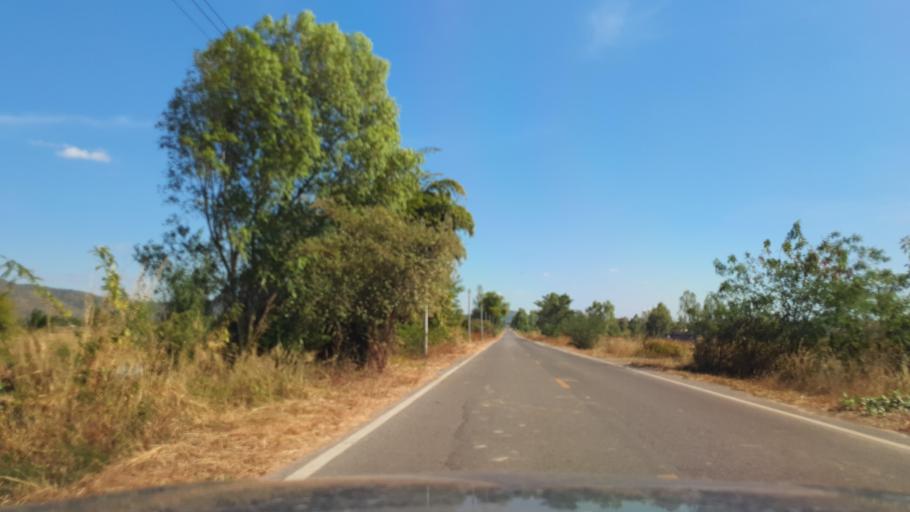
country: TH
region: Kalasin
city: Khao Wong
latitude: 16.7228
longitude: 104.1052
